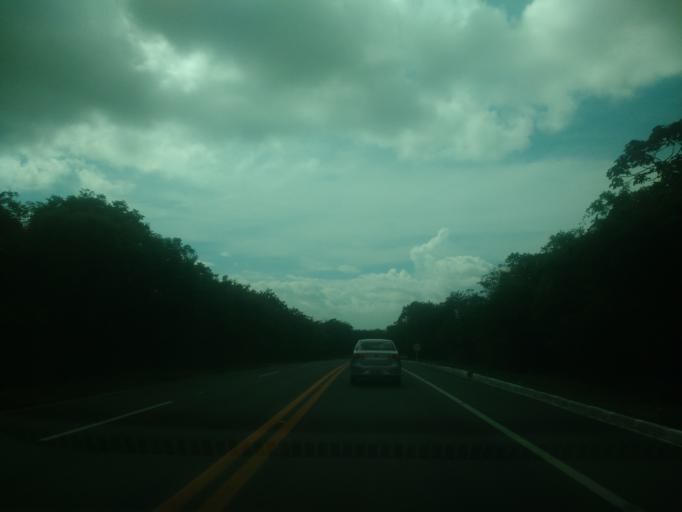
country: BR
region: Alagoas
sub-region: Marechal Deodoro
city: Marechal Deodoro
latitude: -9.6884
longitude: -35.8183
